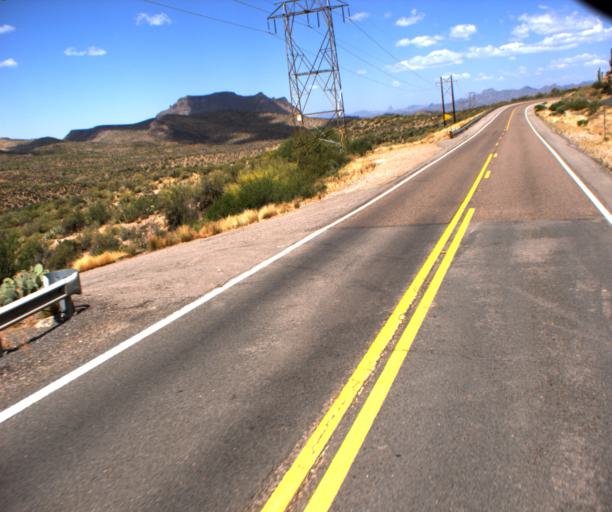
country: US
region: Arizona
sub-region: Pinal County
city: Superior
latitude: 33.2344
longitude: -111.0931
